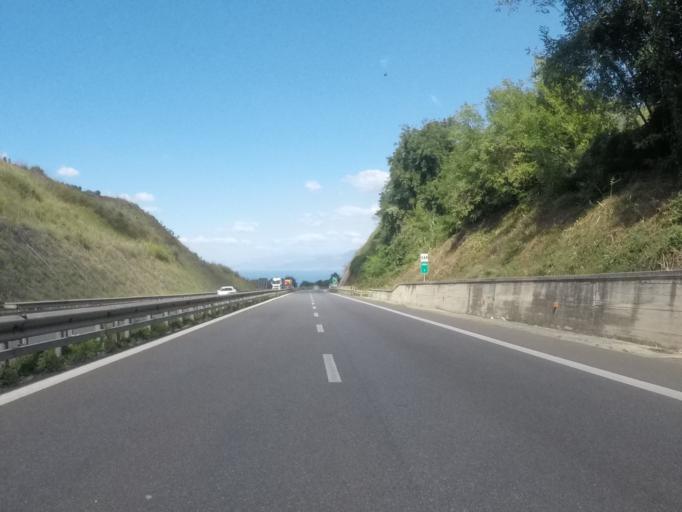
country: IT
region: Calabria
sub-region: Provincia di Vibo-Valentia
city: Sant'Onofrio
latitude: 38.7103
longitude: 16.1539
